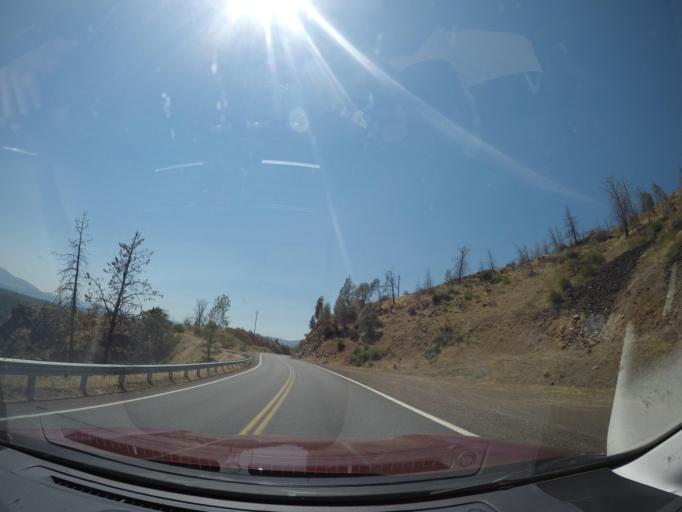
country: US
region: California
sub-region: Shasta County
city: Burney
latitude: 40.9938
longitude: -121.4905
